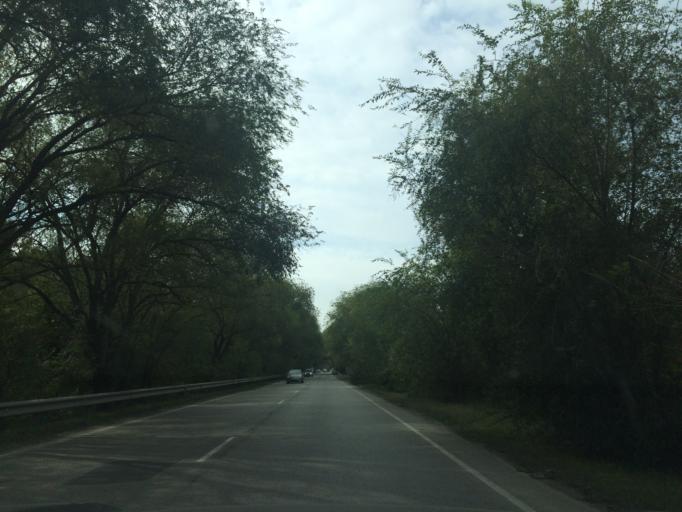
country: RU
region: Rostov
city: Kalinin
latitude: 47.1821
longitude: 39.6047
